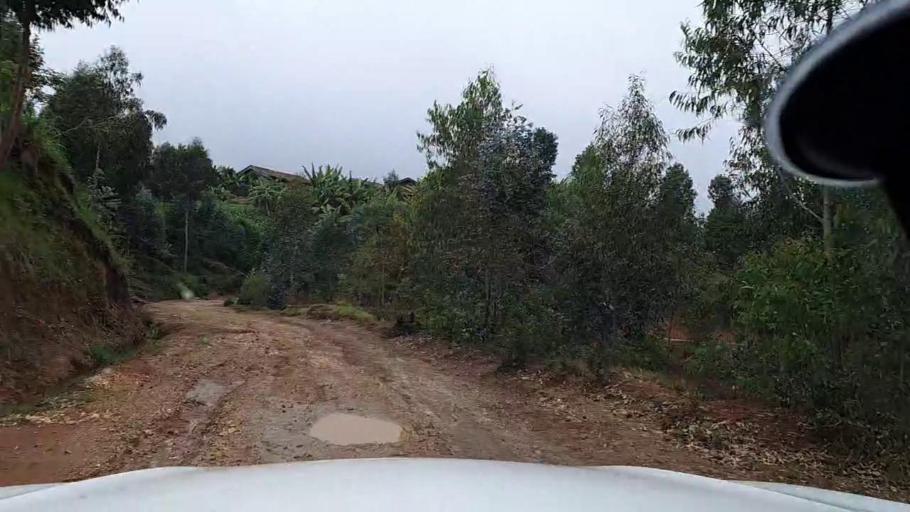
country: RW
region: Western Province
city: Kibuye
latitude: -2.0839
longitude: 29.5097
